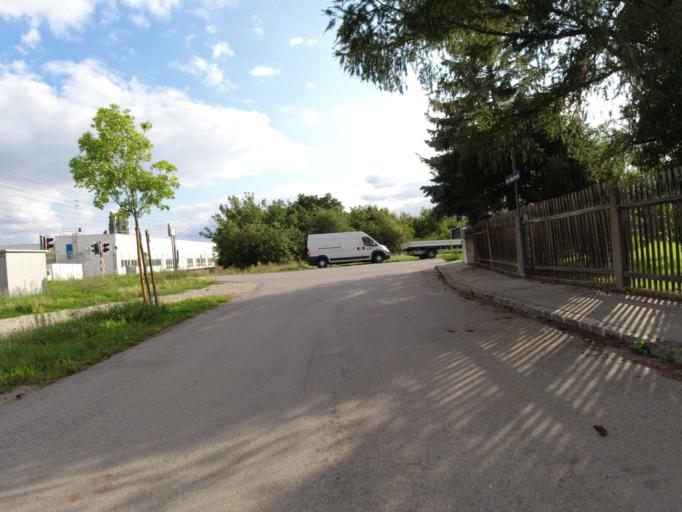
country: AT
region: Lower Austria
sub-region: Politischer Bezirk Baden
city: Traiskirchen
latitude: 48.0104
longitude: 16.2868
